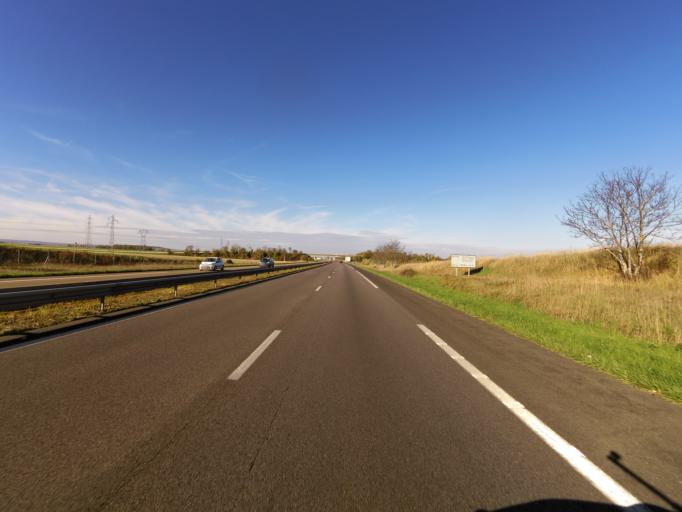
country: FR
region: Champagne-Ardenne
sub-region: Departement de la Marne
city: Sillery
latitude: 49.1900
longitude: 4.1382
